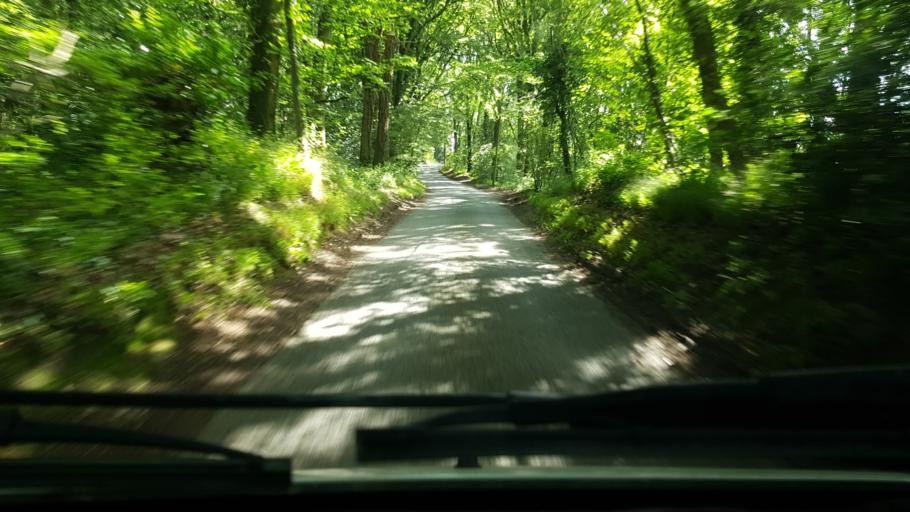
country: GB
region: England
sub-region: Worcestershire
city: Bewdley
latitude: 52.3615
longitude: -2.3254
